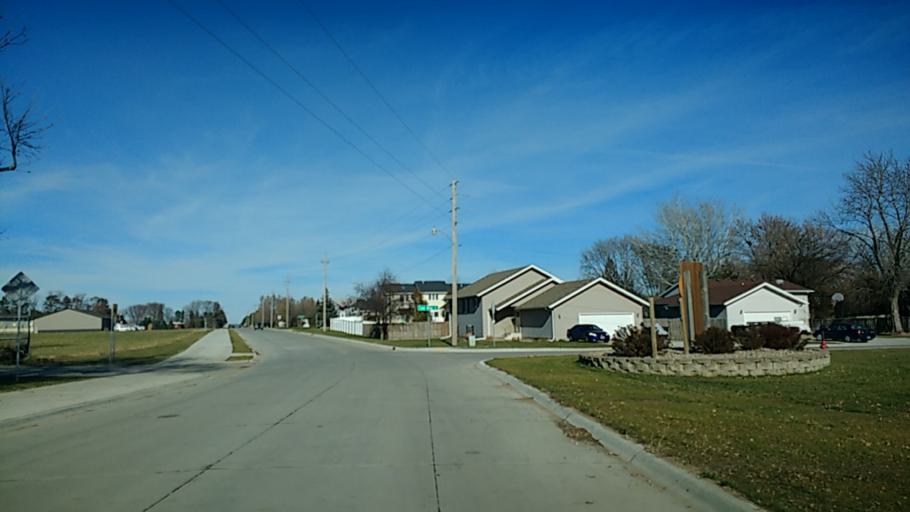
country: US
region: South Dakota
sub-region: Union County
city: North Sioux City
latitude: 42.5415
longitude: -96.5266
